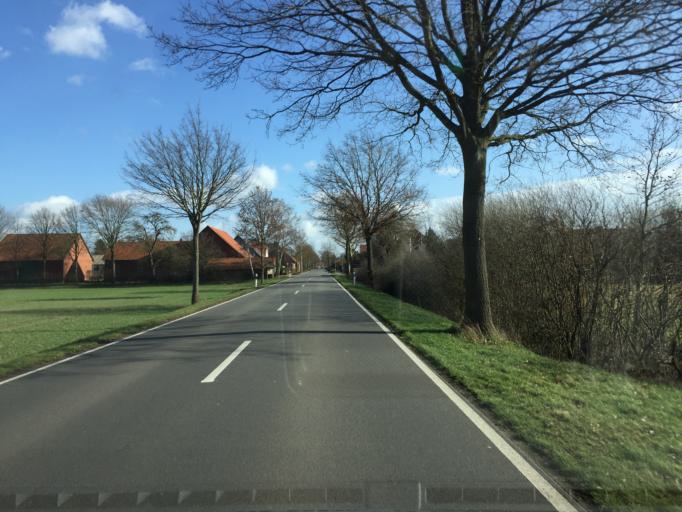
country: DE
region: Lower Saxony
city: Stolzenau
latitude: 52.5372
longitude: 9.0640
